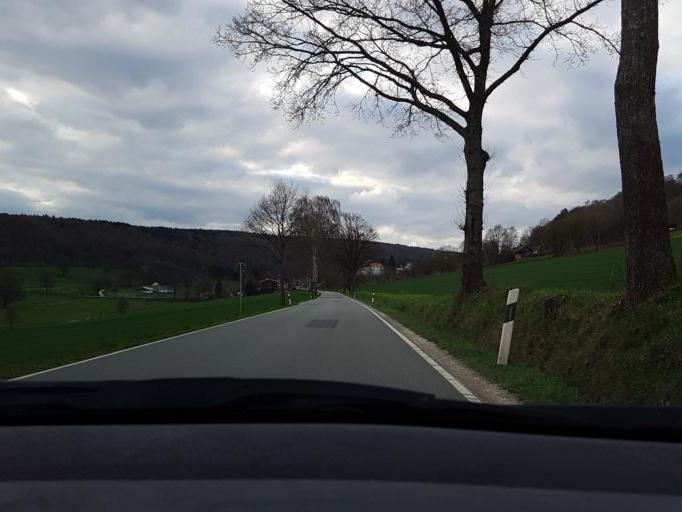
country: DE
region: Lower Saxony
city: Bodenfelde
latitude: 51.6879
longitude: 9.5248
